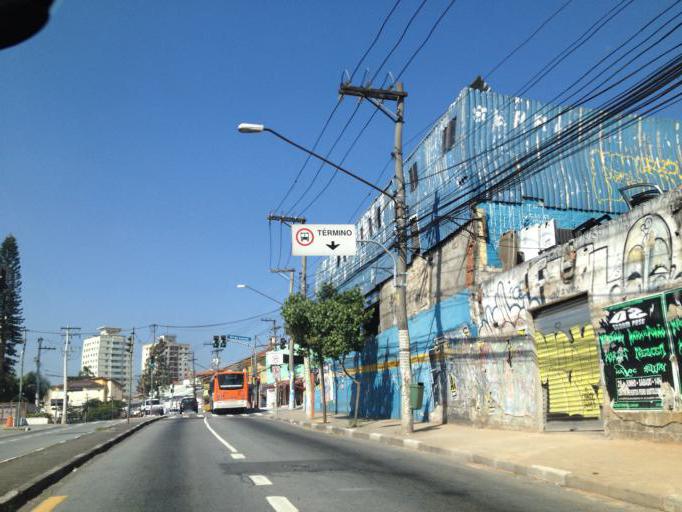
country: BR
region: Sao Paulo
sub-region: Osasco
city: Osasco
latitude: -23.5737
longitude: -46.7363
